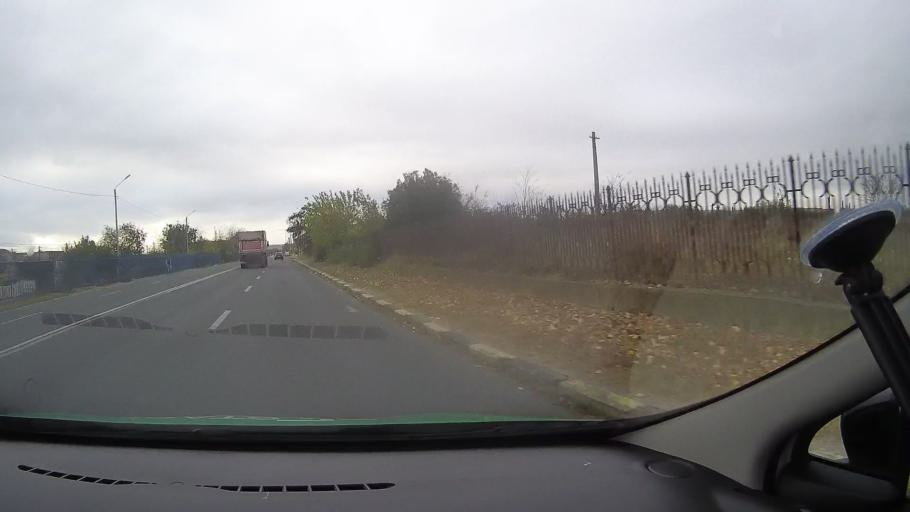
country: RO
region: Constanta
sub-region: Oras Murfatlar
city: Murfatlar
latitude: 44.1717
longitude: 28.4218
